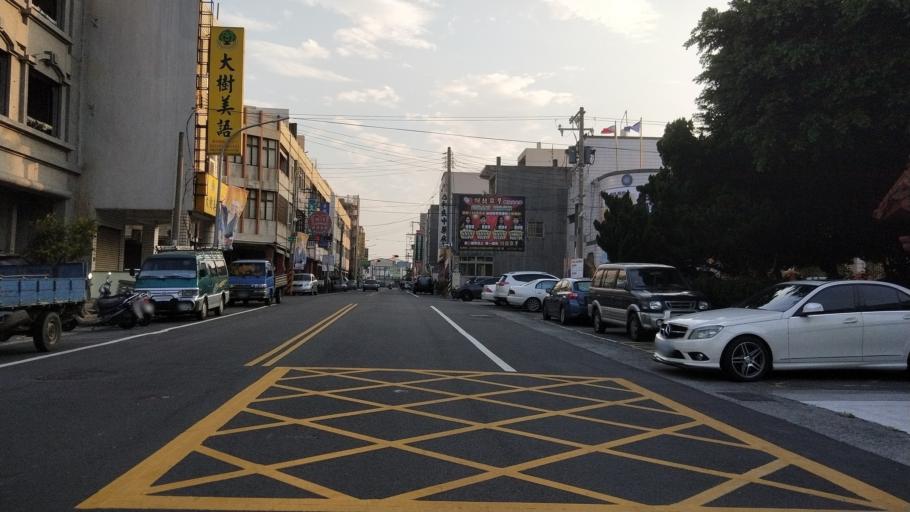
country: TW
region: Taiwan
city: Fengyuan
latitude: 24.4395
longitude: 120.6535
